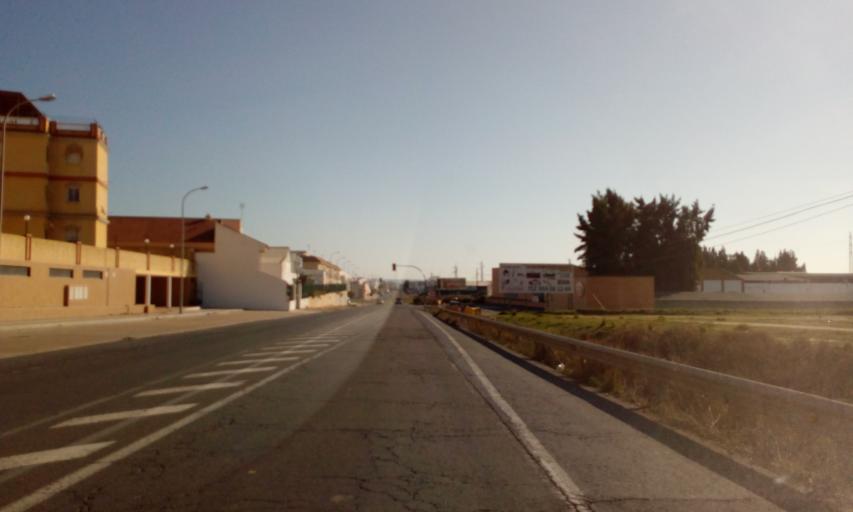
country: ES
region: Andalusia
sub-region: Provincia de Huelva
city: Lepe
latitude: 37.2539
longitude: -7.2145
